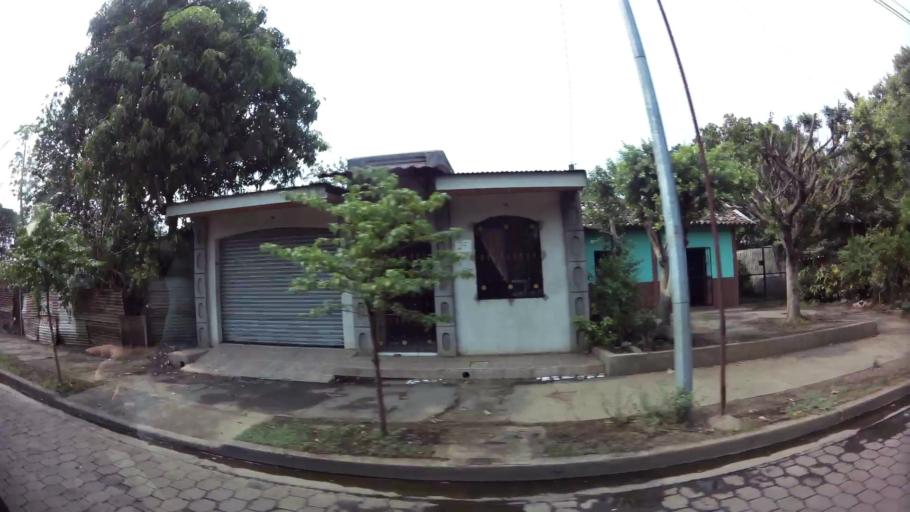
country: NI
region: Chinandega
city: Chinandega
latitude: 12.6279
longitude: -87.1433
